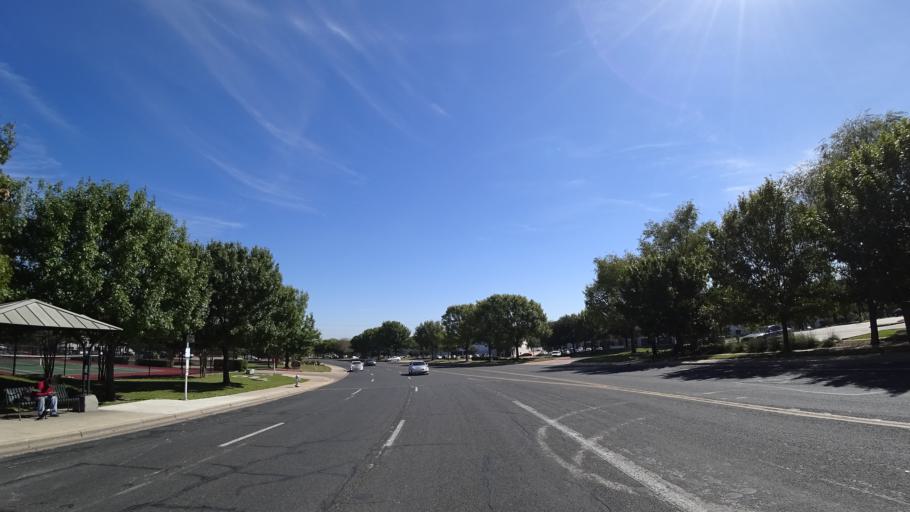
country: US
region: Texas
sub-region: Travis County
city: Austin
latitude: 30.2167
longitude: -97.6898
